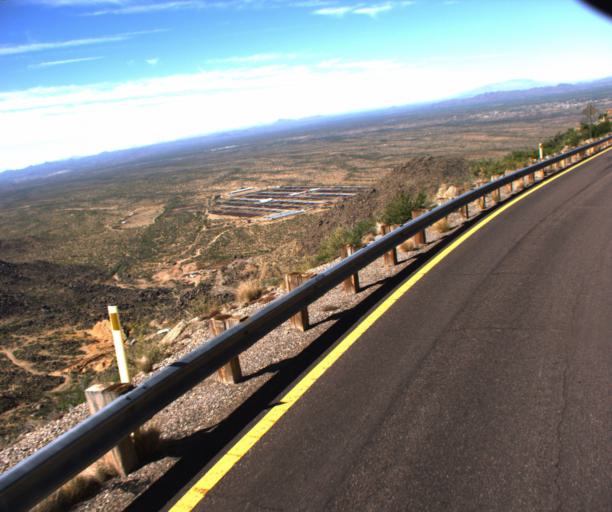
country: US
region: Arizona
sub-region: Yavapai County
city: Congress
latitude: 34.2037
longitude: -112.7735
